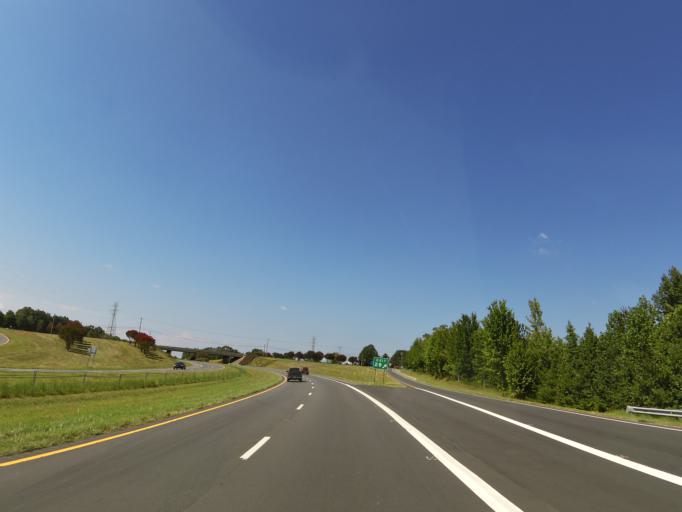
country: US
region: North Carolina
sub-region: Catawba County
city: Maiden
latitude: 35.5252
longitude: -81.2219
